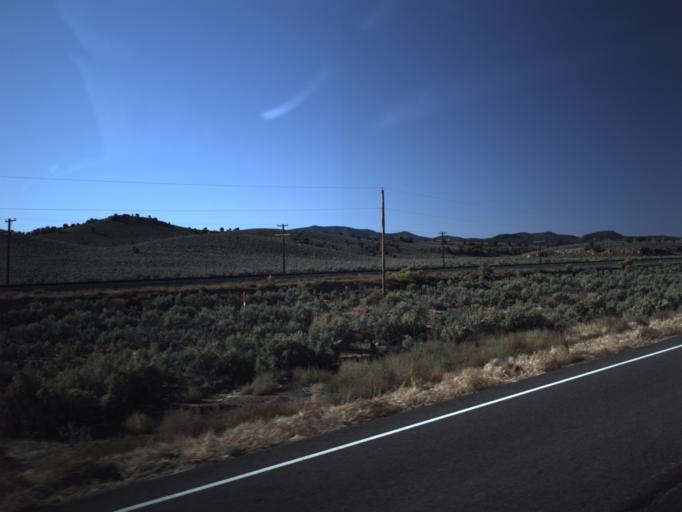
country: US
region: Utah
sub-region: Washington County
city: Enterprise
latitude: 37.7729
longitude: -113.9749
